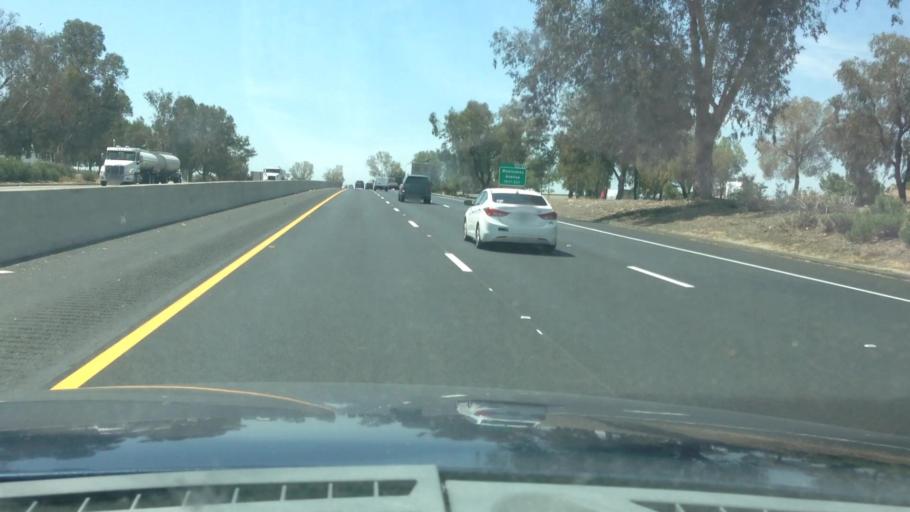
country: US
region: California
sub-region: Kern County
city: Delano
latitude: 35.7594
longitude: -119.2487
